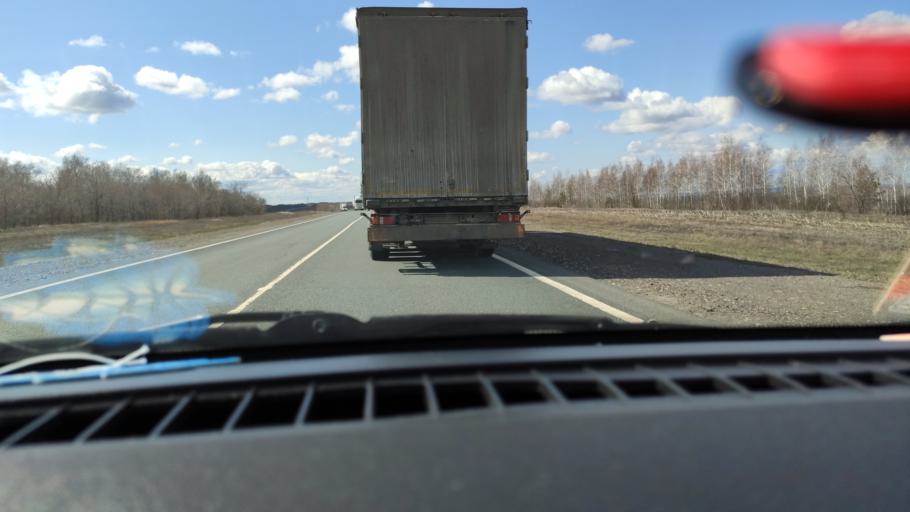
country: RU
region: Samara
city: Syzran'
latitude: 52.8556
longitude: 48.2600
